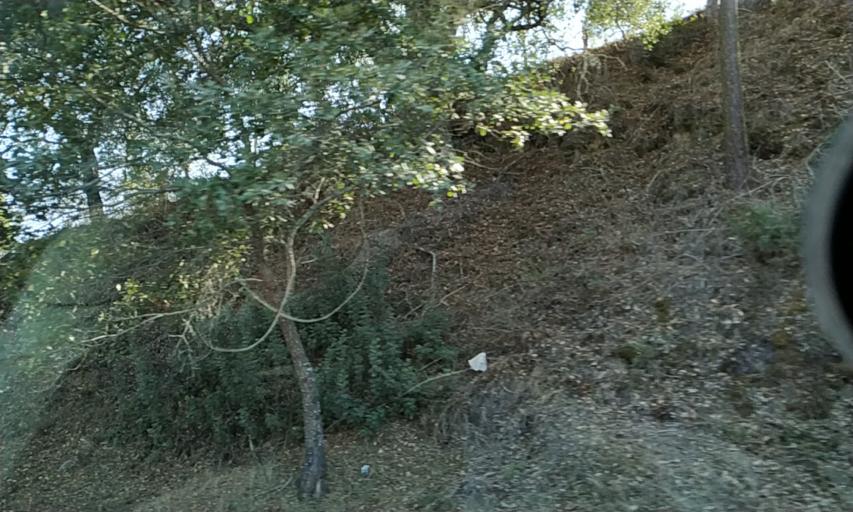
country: PT
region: Santarem
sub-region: Benavente
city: Poceirao
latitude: 38.7666
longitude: -8.6209
